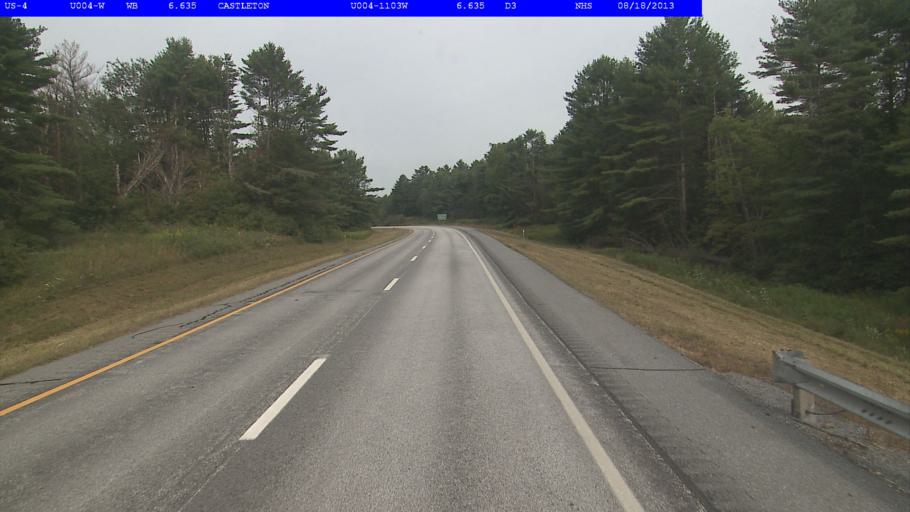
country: US
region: Vermont
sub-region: Rutland County
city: Castleton
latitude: 43.6218
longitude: -73.1857
